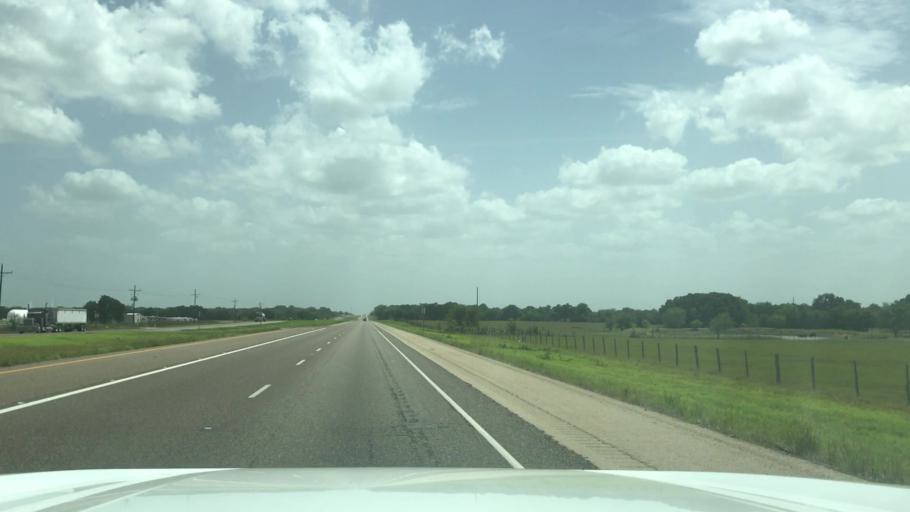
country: US
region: Texas
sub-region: Robertson County
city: Calvert
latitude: 31.0758
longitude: -96.7133
